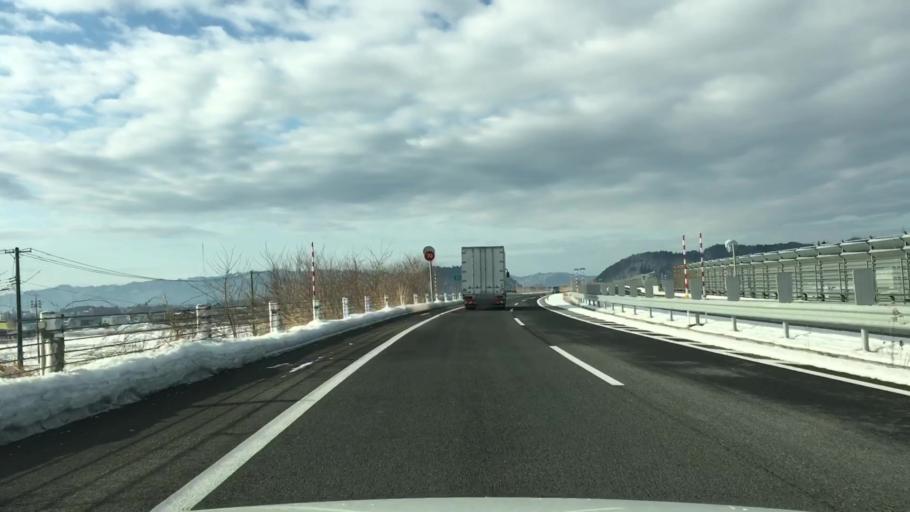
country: JP
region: Akita
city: Odate
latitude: 40.2915
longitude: 140.5502
